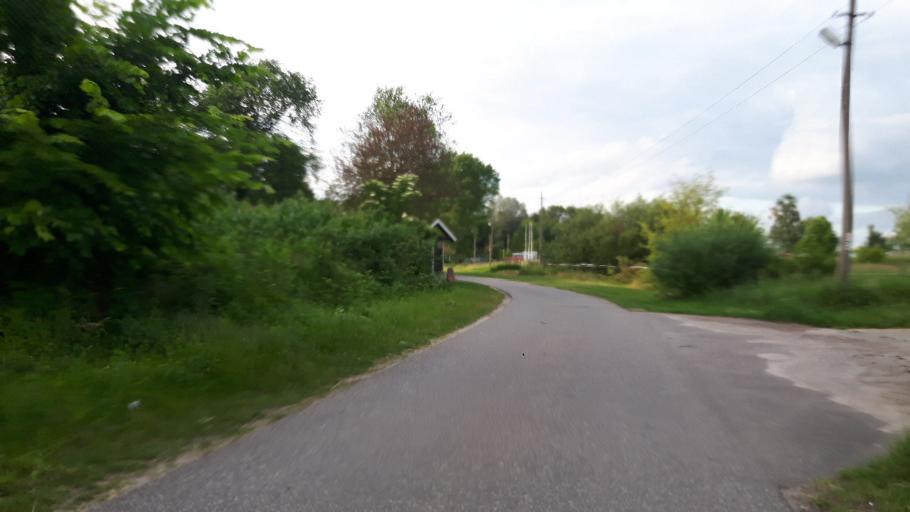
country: DE
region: Brandenburg
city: Gartz
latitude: 53.2093
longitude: 14.3994
